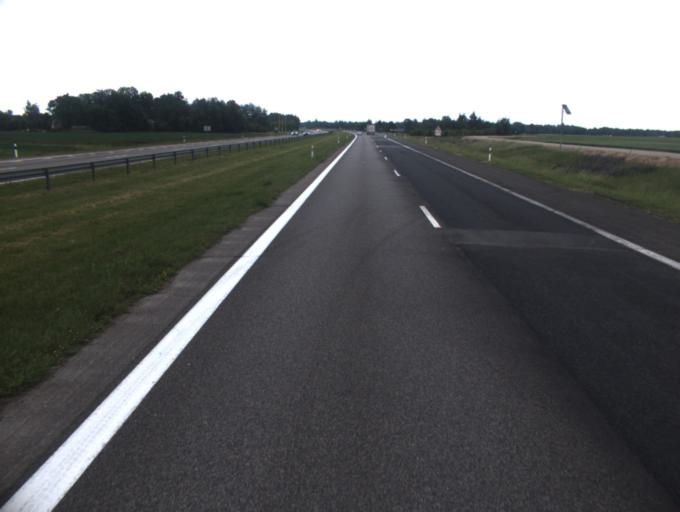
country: LT
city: Skaudvile
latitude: 55.4265
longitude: 22.7586
